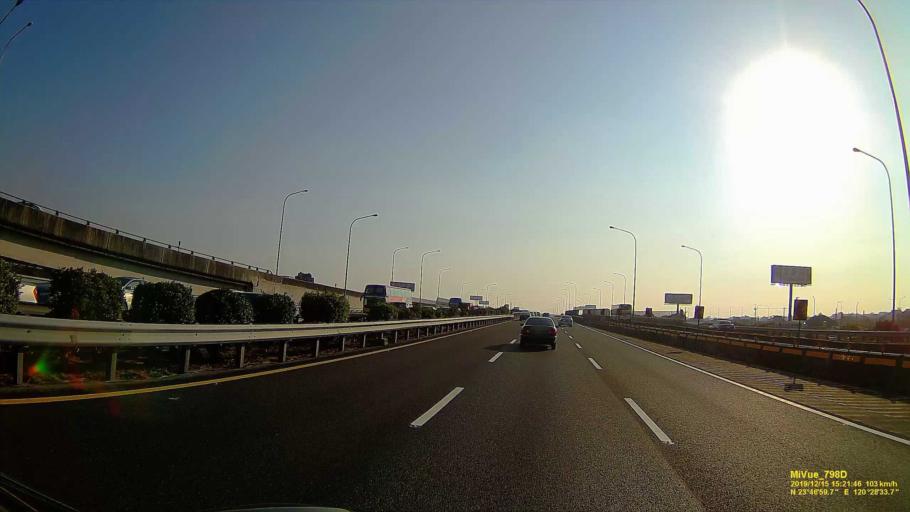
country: TW
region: Taiwan
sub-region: Yunlin
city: Douliu
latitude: 23.7826
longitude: 120.4757
